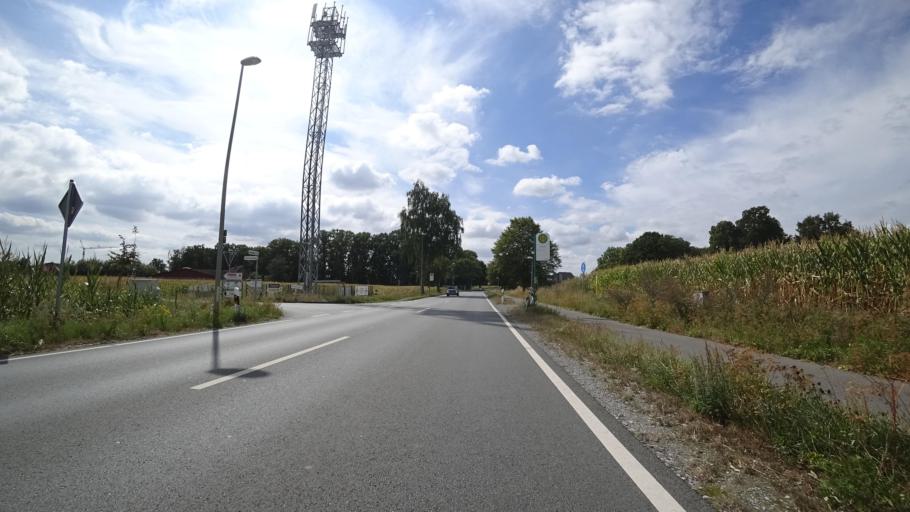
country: DE
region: North Rhine-Westphalia
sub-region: Regierungsbezirk Detmold
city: Guetersloh
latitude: 51.9155
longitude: 8.4411
